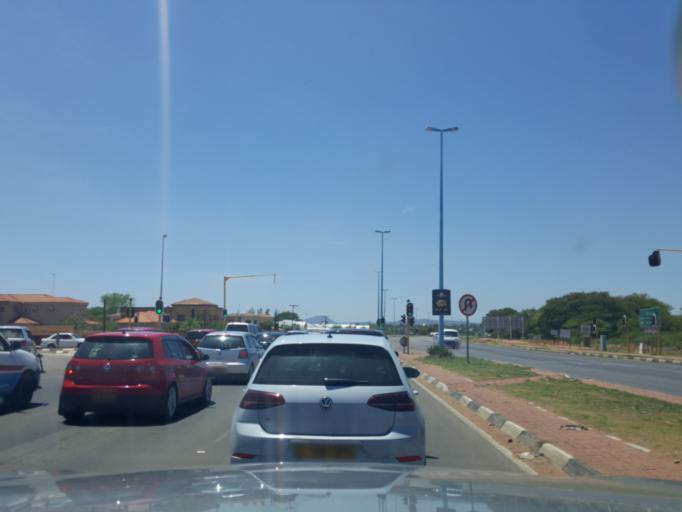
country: BW
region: Kweneng
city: Mogoditshane
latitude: -24.6352
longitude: 25.8770
